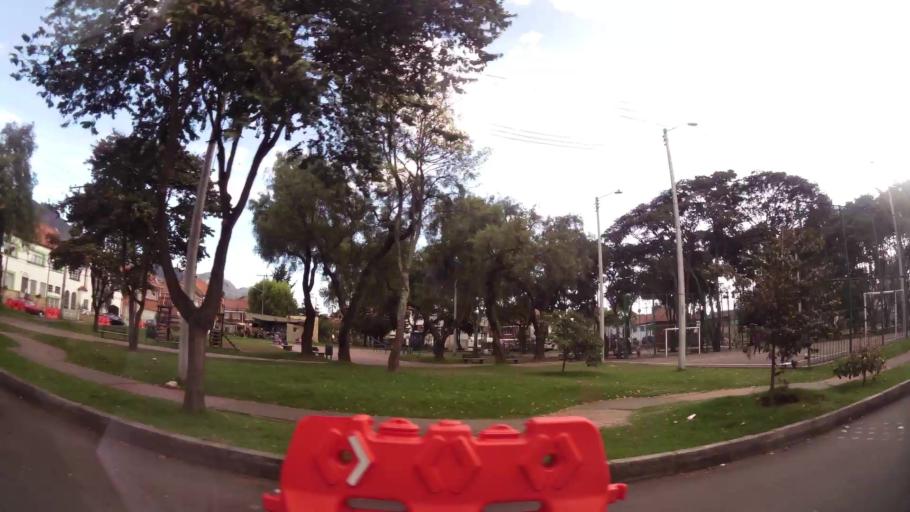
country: CO
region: Bogota D.C.
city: Bogota
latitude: 4.6486
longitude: -74.0689
